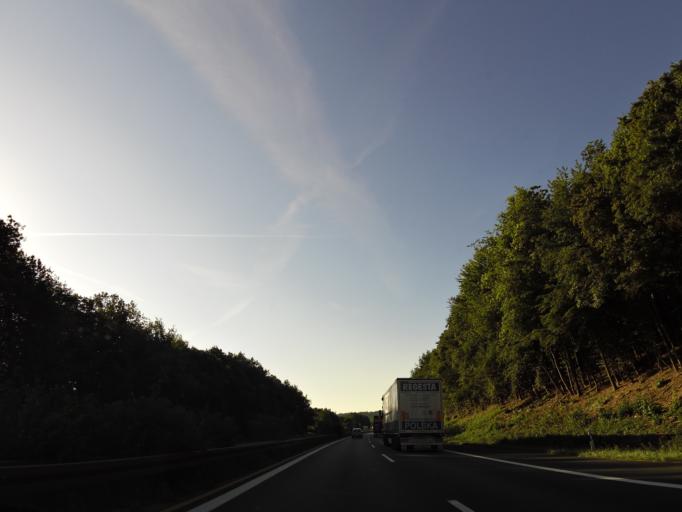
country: DE
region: Bavaria
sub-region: Upper Franconia
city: Schlusselfeld
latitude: 49.7389
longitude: 10.6544
